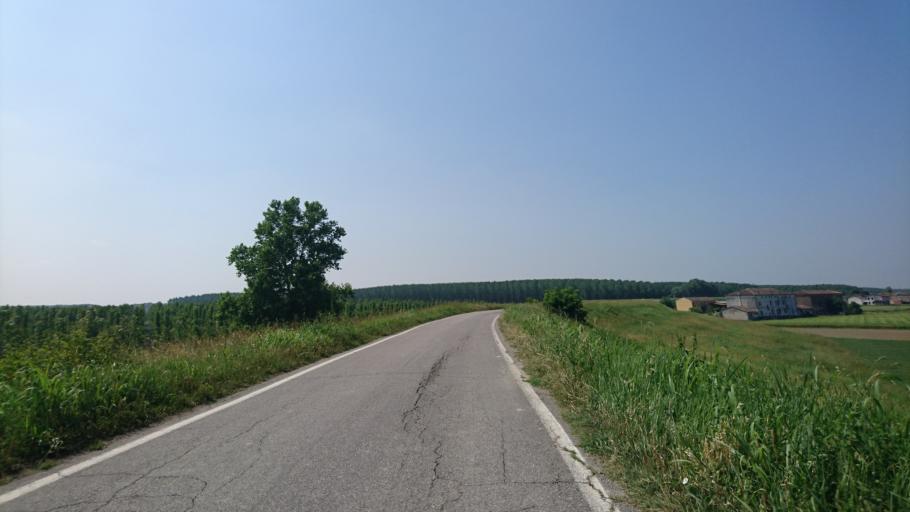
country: IT
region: Lombardy
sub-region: Provincia di Mantova
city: Serravalle a Po
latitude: 45.0697
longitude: 11.0992
